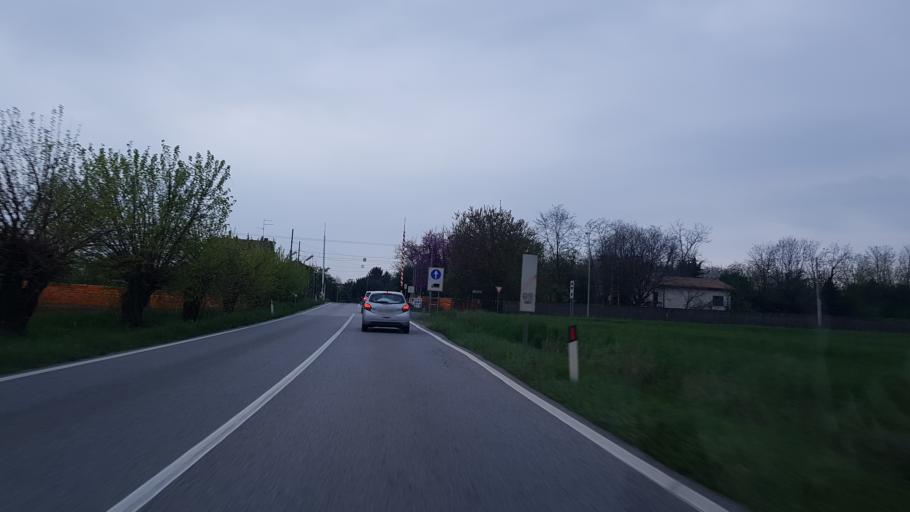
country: IT
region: Friuli Venezia Giulia
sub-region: Provincia di Udine
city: Palmanova
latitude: 45.9004
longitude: 13.2998
